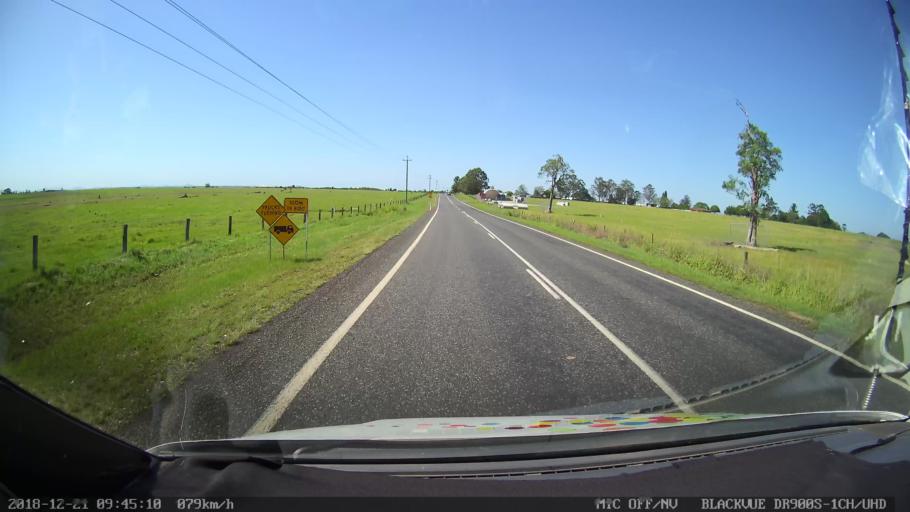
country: AU
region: New South Wales
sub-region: Clarence Valley
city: Grafton
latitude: -29.6253
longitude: 152.9290
